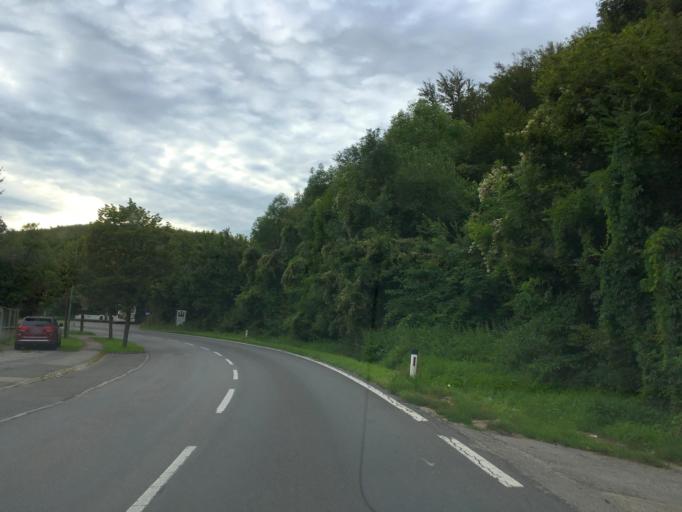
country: AT
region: Lower Austria
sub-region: Politischer Bezirk Tulln
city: Wordern
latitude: 48.3180
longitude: 16.2352
